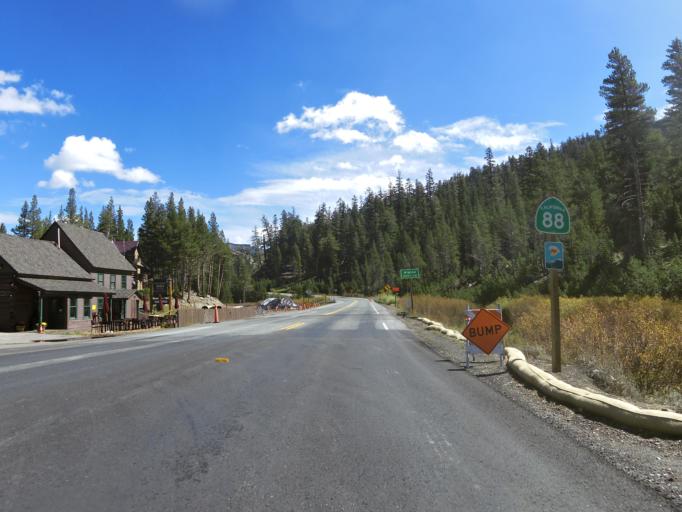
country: US
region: California
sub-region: El Dorado County
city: South Lake Tahoe
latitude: 38.7026
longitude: -120.0728
